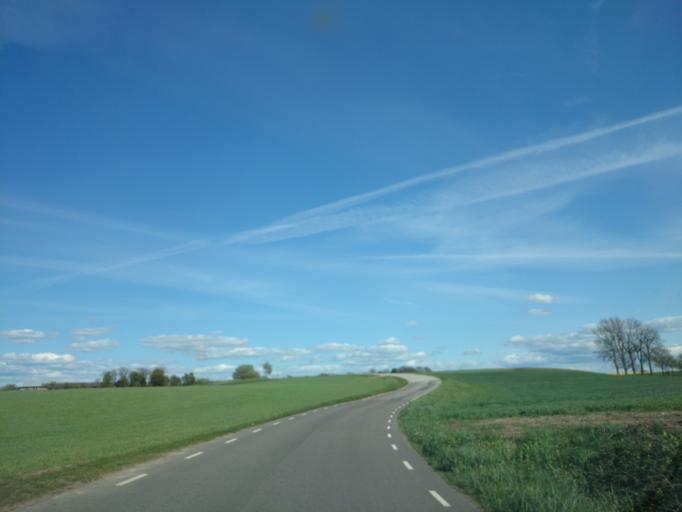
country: SE
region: Skane
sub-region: Kavlinge Kommun
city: Kaevlinge
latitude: 55.7855
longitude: 13.1253
